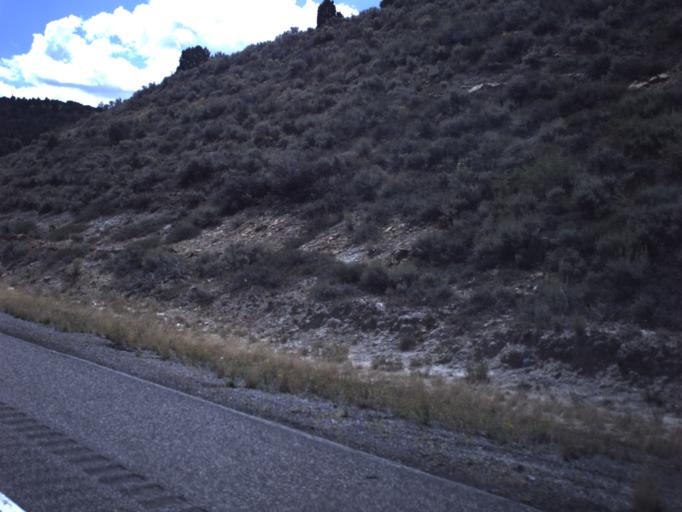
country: US
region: Utah
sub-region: Sevier County
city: Salina
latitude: 38.8069
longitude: -111.5307
